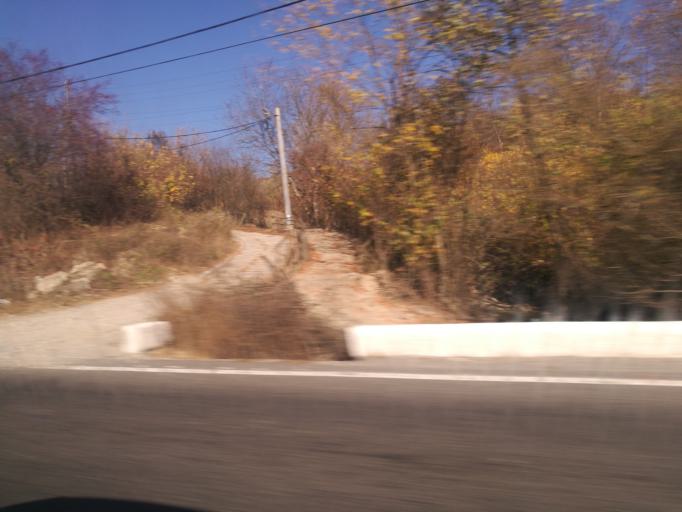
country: RO
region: Prahova
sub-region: Oras Breaza
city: Breaza
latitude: 45.1881
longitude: 25.6783
